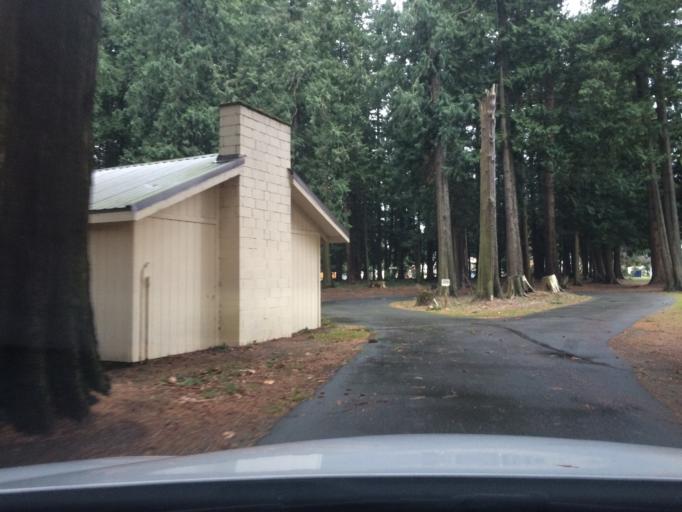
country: US
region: Washington
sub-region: Whatcom County
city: Lynden
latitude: 48.9492
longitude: -122.4501
